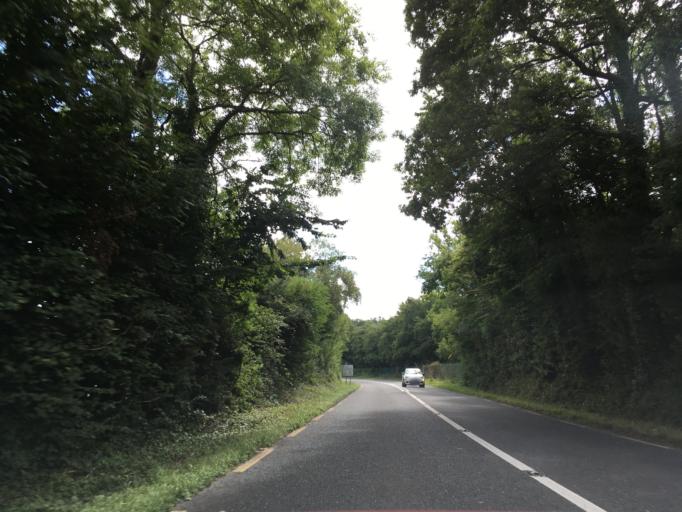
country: IE
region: Munster
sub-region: County Cork
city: Carrigaline
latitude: 51.8104
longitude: -8.3634
